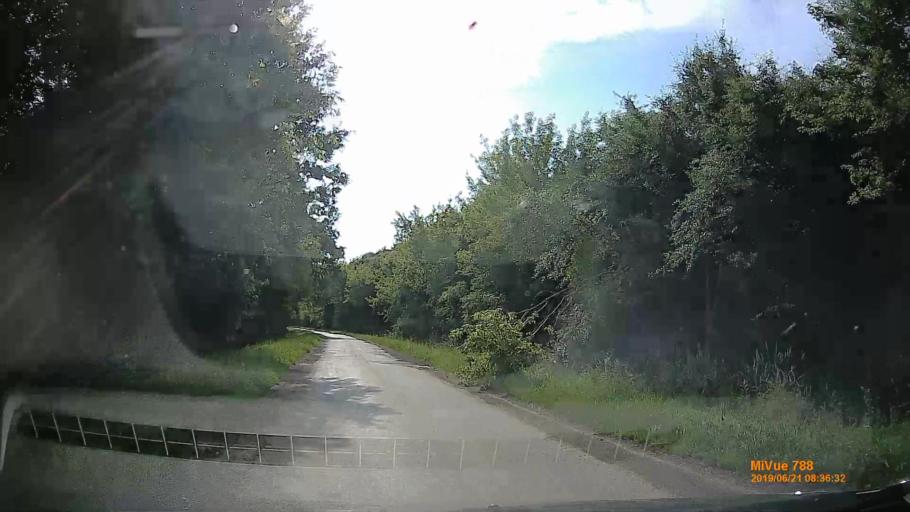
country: HU
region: Baranya
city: Buekkoesd
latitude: 46.1728
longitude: 17.9078
